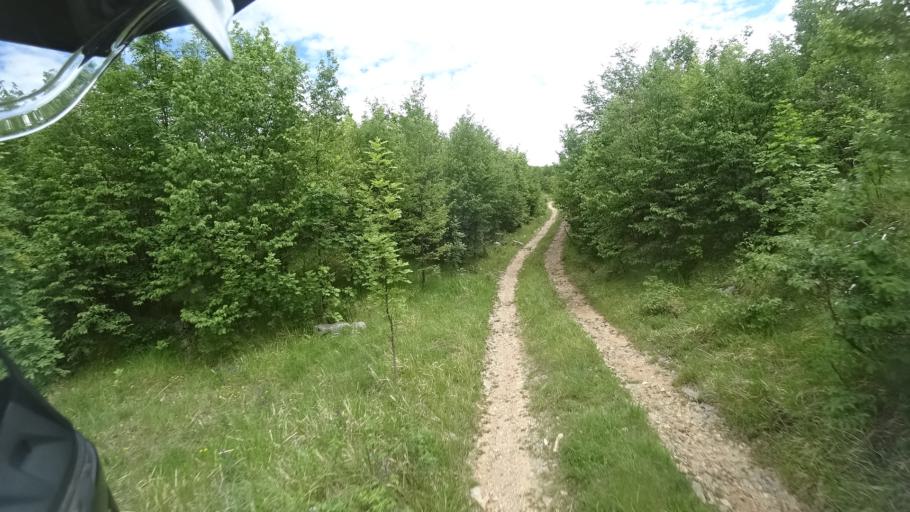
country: HR
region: Splitsko-Dalmatinska
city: Hrvace
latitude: 43.8845
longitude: 16.5861
